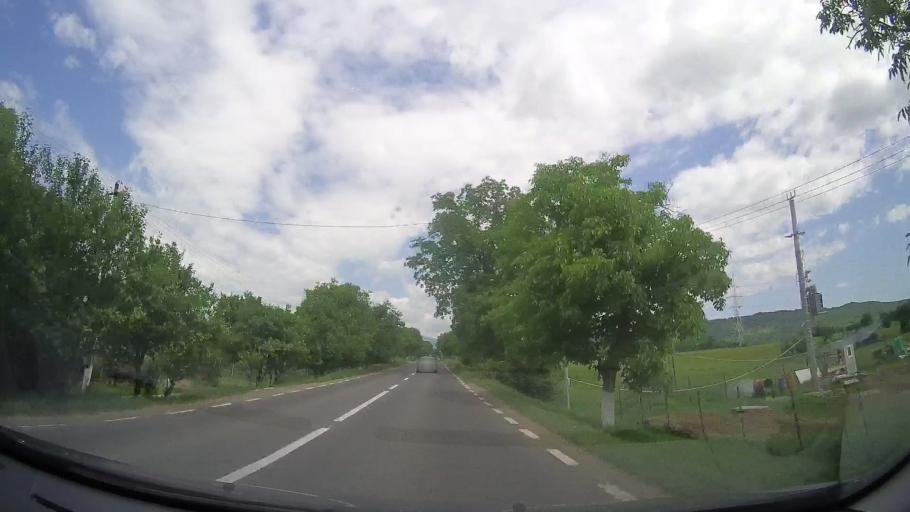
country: RO
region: Prahova
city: Drajna de Jos
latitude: 45.2362
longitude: 26.0290
